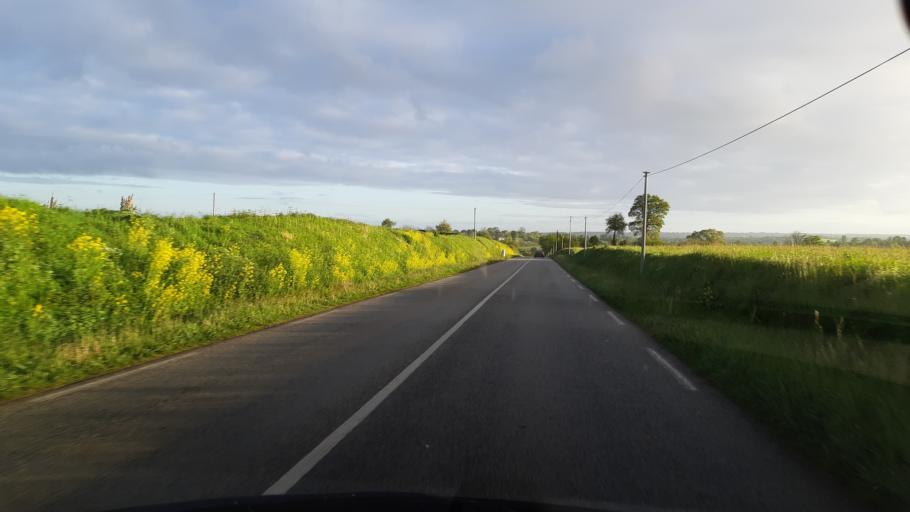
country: FR
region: Lower Normandy
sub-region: Departement de la Manche
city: Agneaux
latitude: 49.0591
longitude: -1.1332
